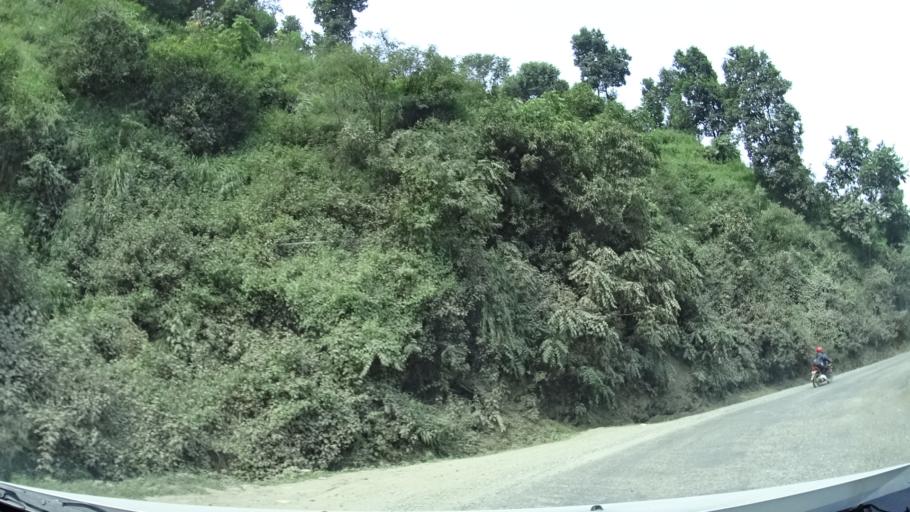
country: NP
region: Central Region
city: Kirtipur
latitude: 27.7090
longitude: 85.1912
